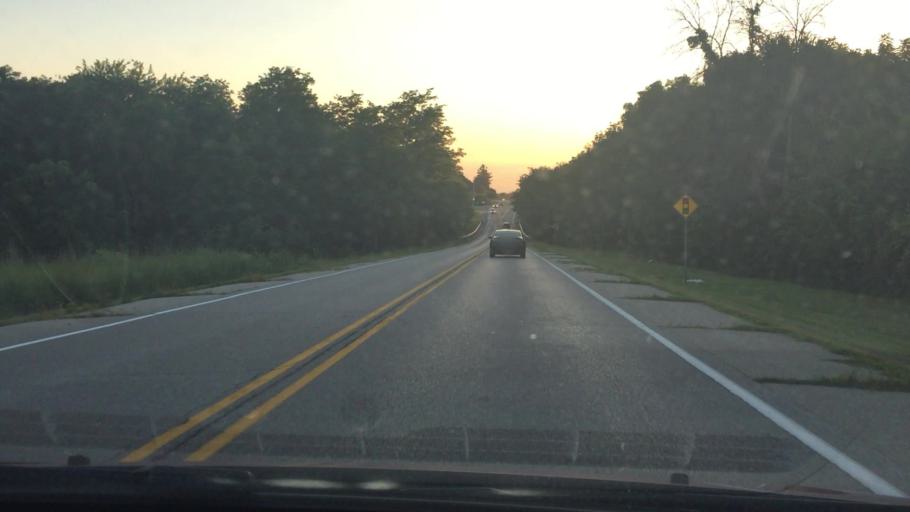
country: US
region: Iowa
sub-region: Muscatine County
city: Muscatine
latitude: 41.4361
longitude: -91.0861
